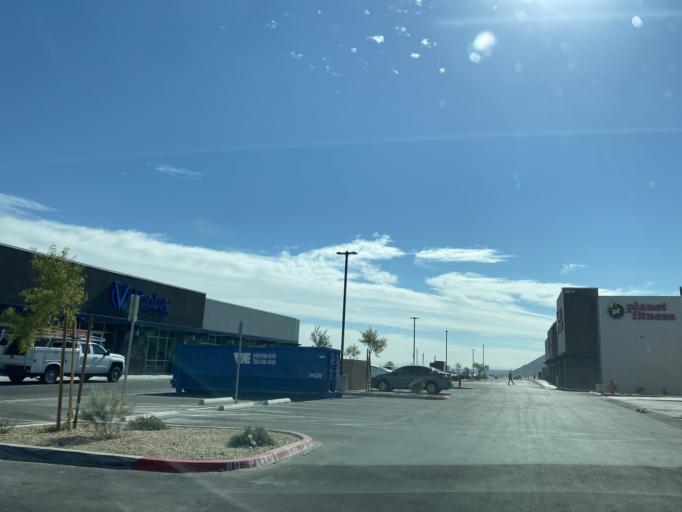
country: US
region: Nevada
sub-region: Clark County
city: Summerlin South
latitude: 36.2842
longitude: -115.3123
